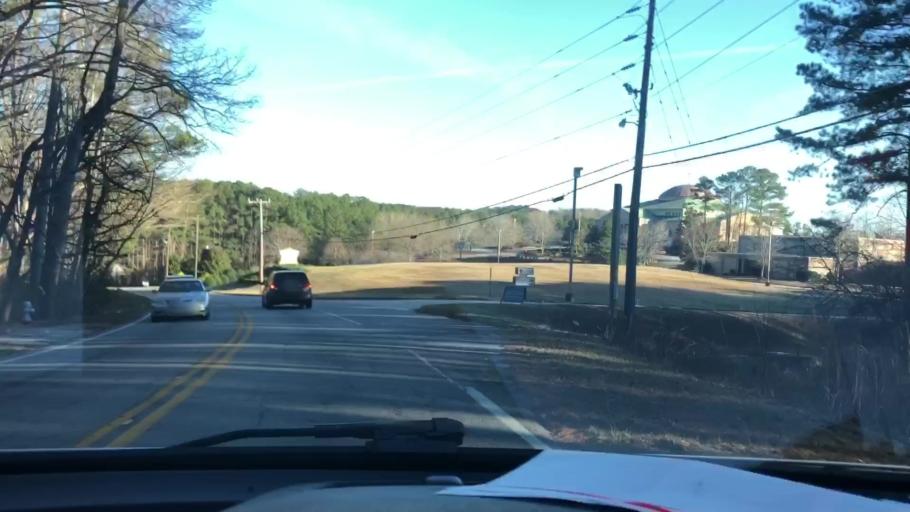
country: US
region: Georgia
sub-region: Gwinnett County
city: Mountain Park
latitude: 33.8299
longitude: -84.1437
